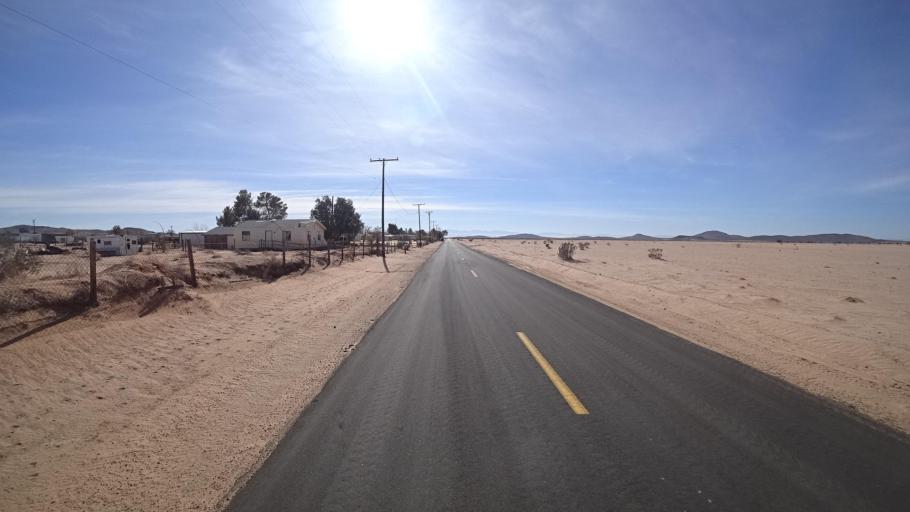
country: US
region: California
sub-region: Kern County
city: North Edwards
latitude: 35.0944
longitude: -117.7926
